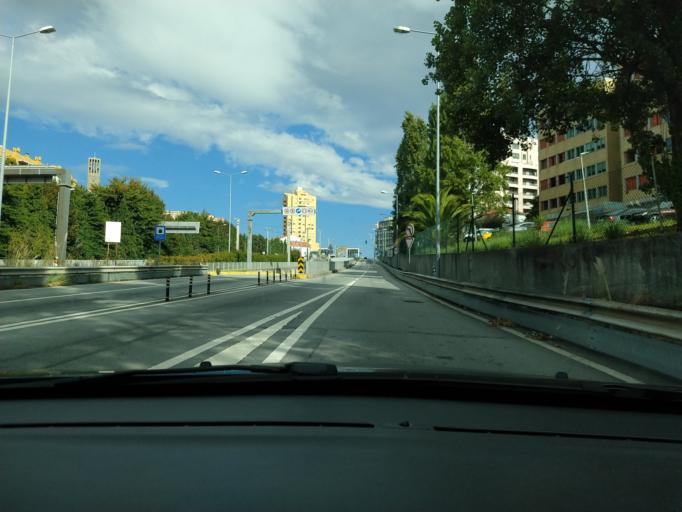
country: PT
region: Porto
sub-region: Vila Nova de Gaia
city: Vilar de Andorinho
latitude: 41.1128
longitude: -8.6067
